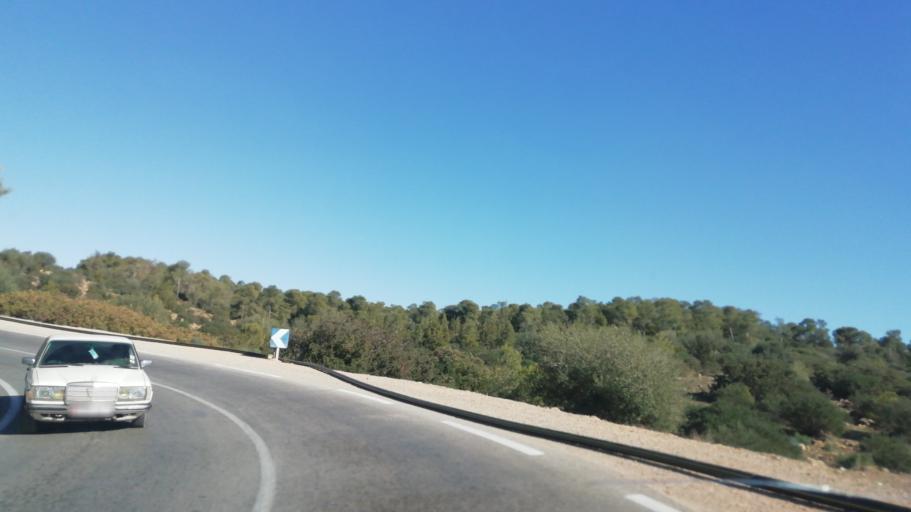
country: DZ
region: Tlemcen
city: Beni Mester
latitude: 34.8126
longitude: -1.6200
